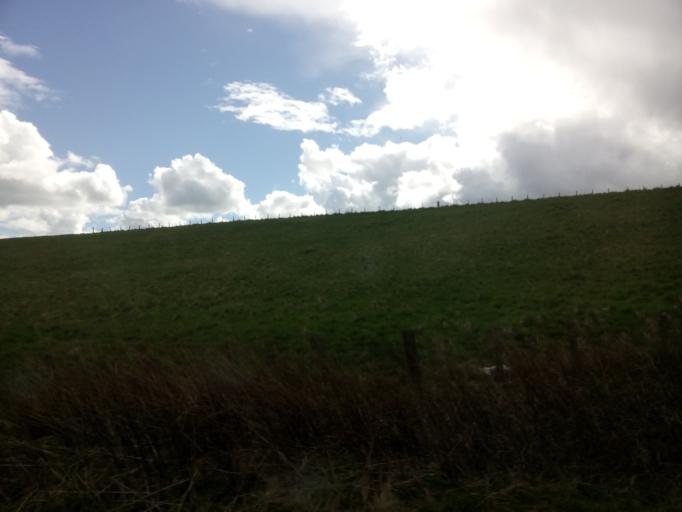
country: GB
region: Scotland
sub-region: The Scottish Borders
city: Chirnside
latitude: 55.8680
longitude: -2.2722
